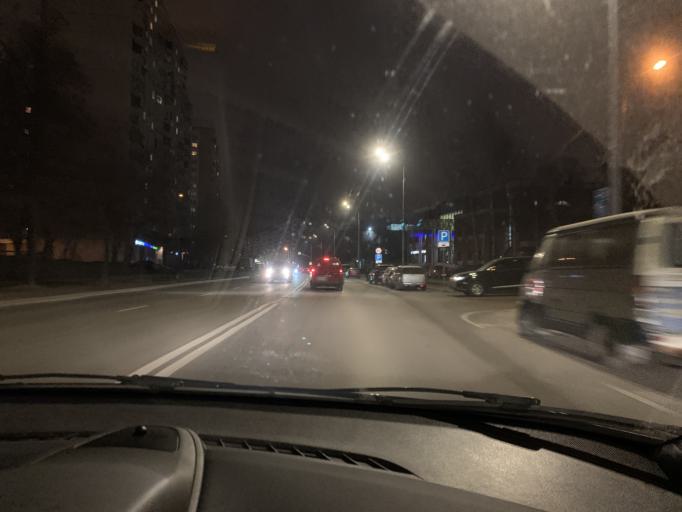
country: RU
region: Moscow
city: Likhobory
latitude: 55.8587
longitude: 37.5678
